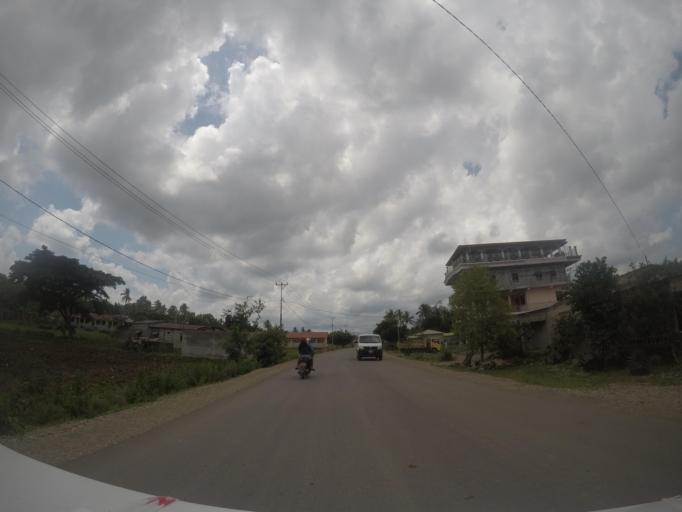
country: TL
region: Baucau
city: Baucau
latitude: -8.5442
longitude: 126.4131
